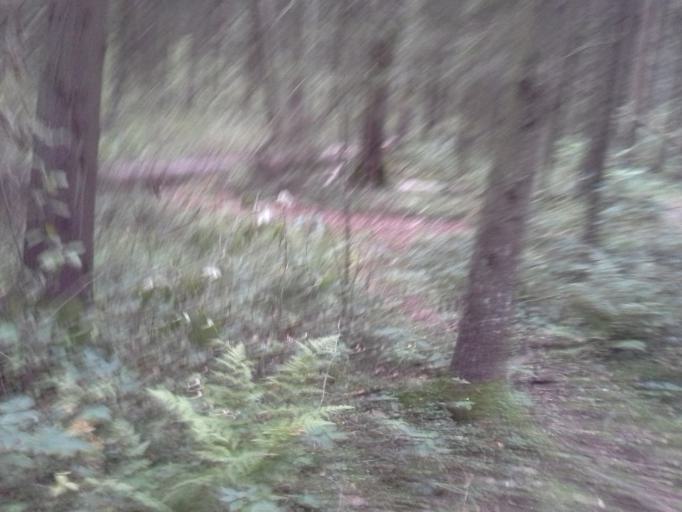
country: RU
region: Moskovskaya
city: Krasnoznamensk
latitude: 55.6199
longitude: 37.0651
